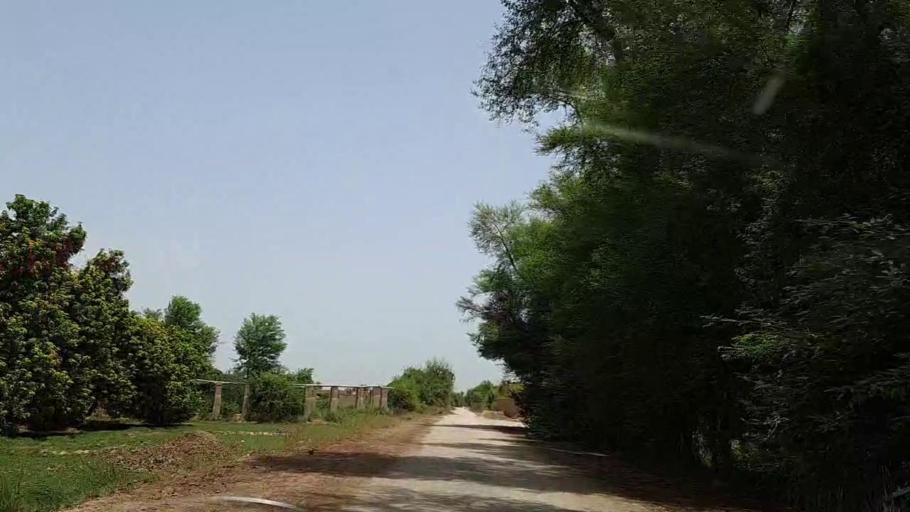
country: PK
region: Sindh
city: Tharu Shah
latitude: 26.9546
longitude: 68.0268
